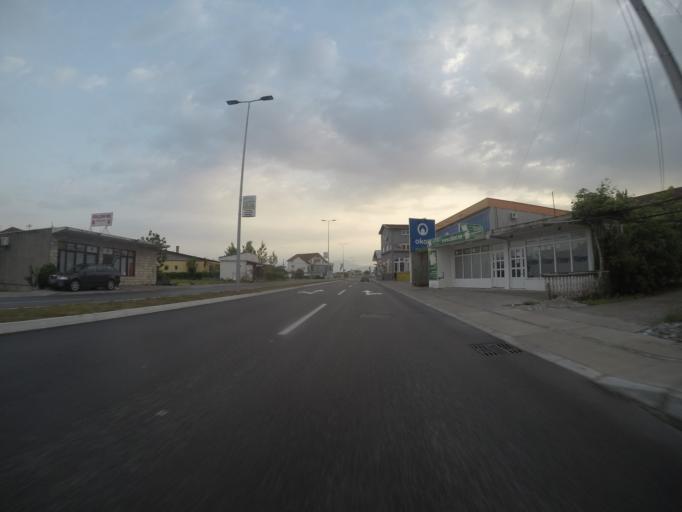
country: ME
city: Mojanovici
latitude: 42.3616
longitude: 19.2254
